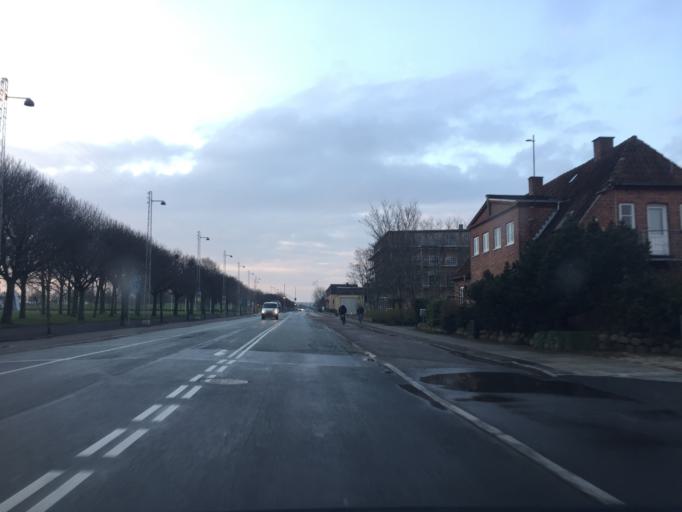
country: DK
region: Capital Region
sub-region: Tarnby Kommune
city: Tarnby
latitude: 55.6410
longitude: 12.6464
